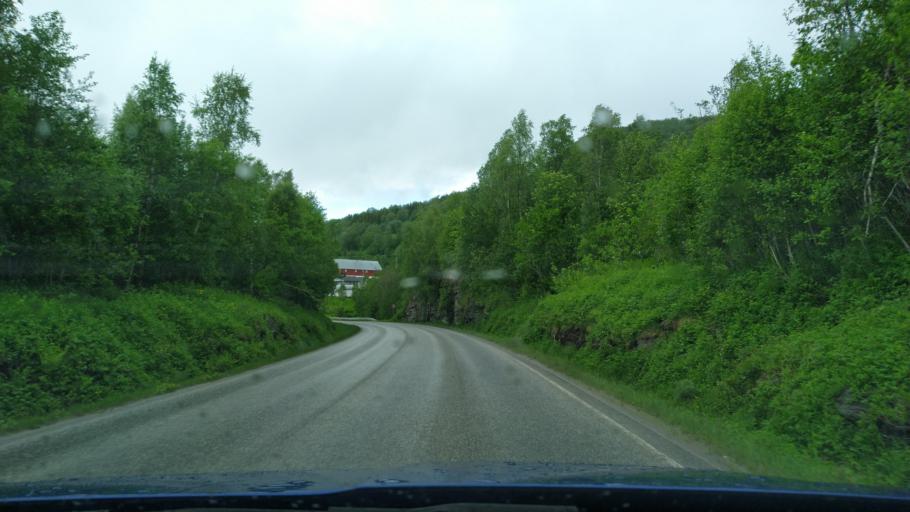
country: NO
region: Troms
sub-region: Sorreisa
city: Sorreisa
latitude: 69.1572
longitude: 18.1604
